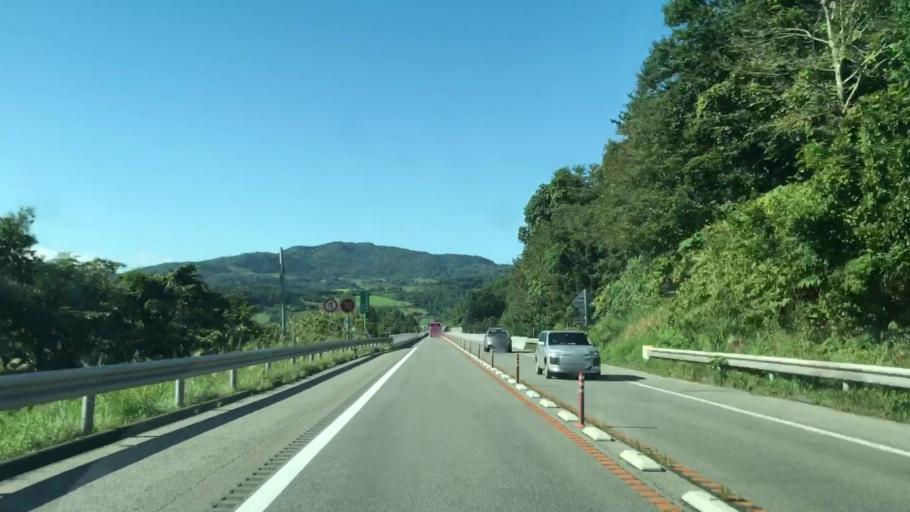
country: JP
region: Hokkaido
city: Date
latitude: 42.5361
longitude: 140.7976
